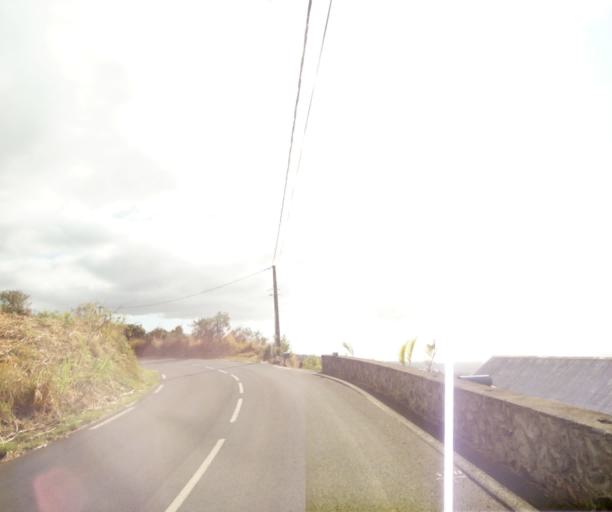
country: RE
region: Reunion
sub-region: Reunion
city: Saint-Paul
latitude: -21.0202
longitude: 55.3138
